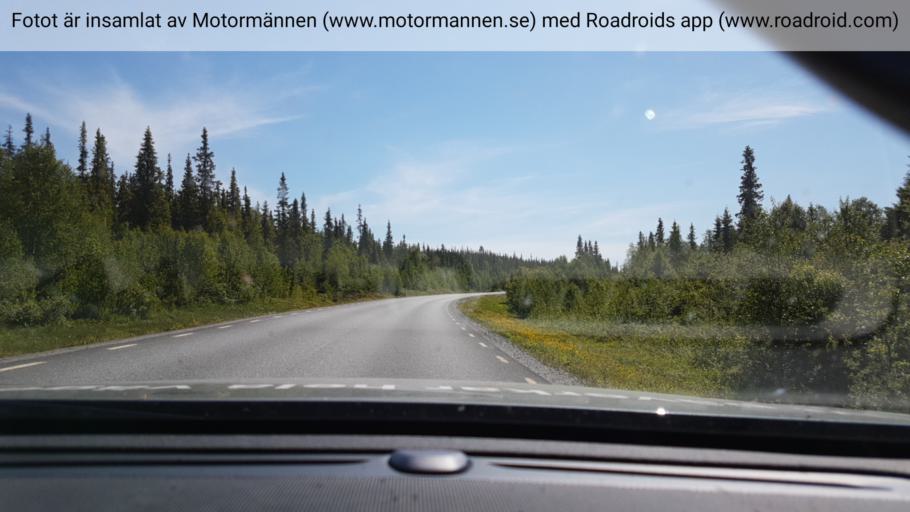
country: SE
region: Vaesterbotten
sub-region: Vilhelmina Kommun
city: Sjoberg
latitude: 64.8093
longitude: 15.2684
